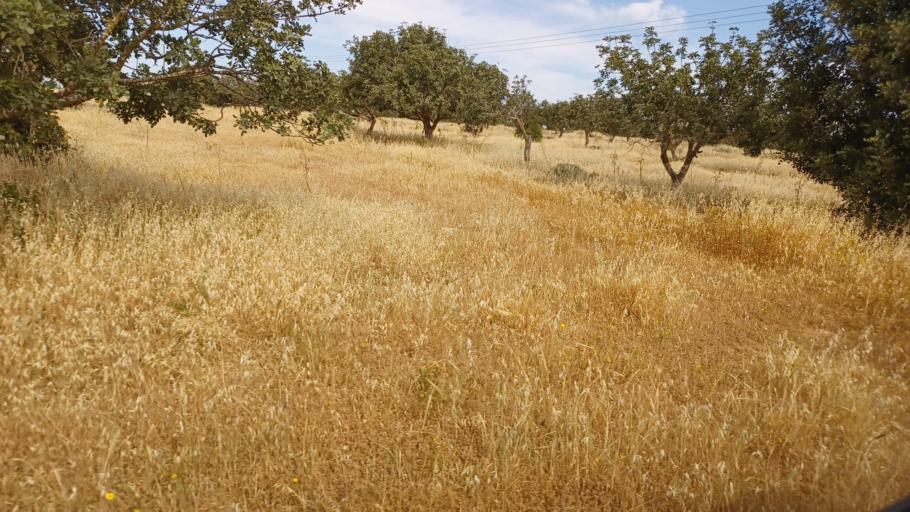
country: CY
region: Lefkosia
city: Kokkinotrimithia
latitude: 35.1621
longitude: 33.1736
